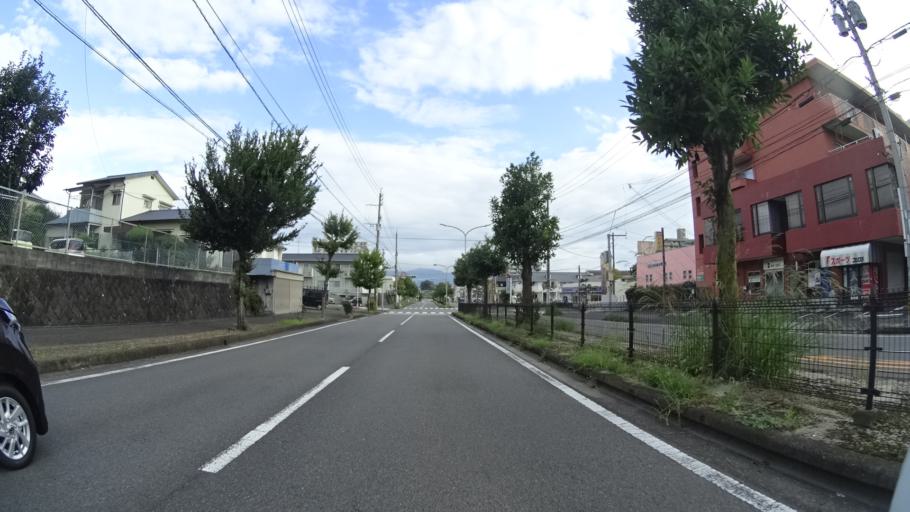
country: JP
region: Oita
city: Beppu
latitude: 33.3018
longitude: 131.4950
